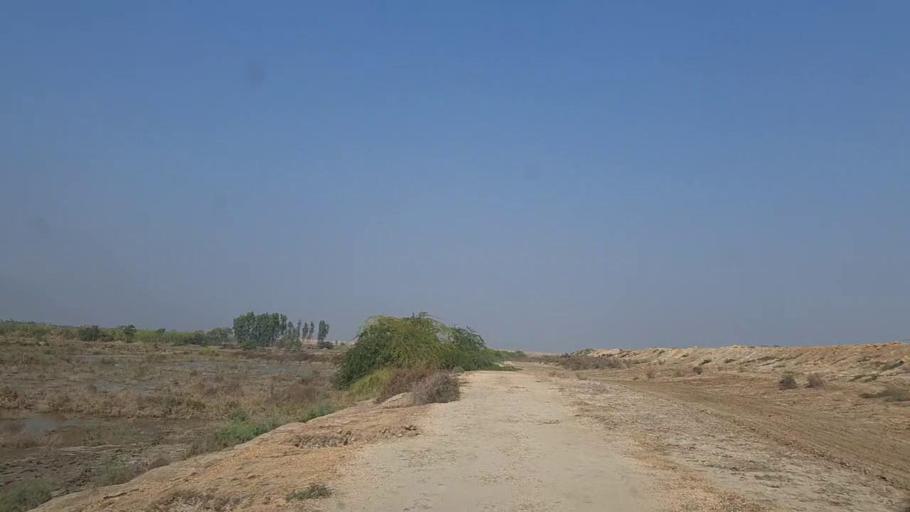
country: PK
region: Sindh
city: Thatta
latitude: 24.6661
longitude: 67.9247
